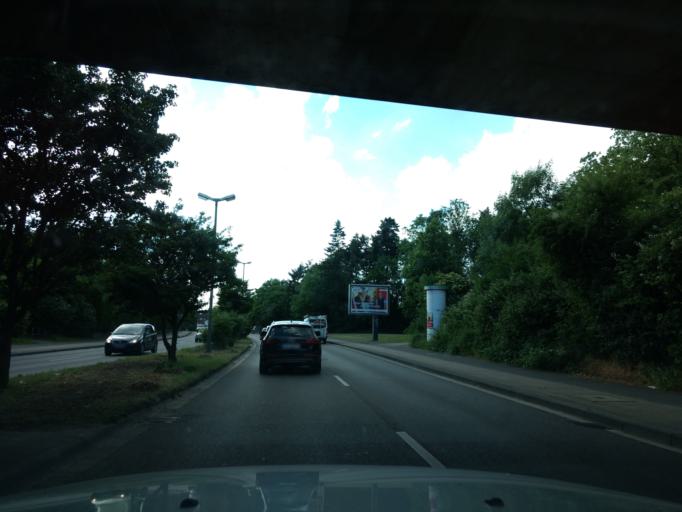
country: DE
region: North Rhine-Westphalia
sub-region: Regierungsbezirk Dusseldorf
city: Neuss
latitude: 51.1840
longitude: 6.6766
